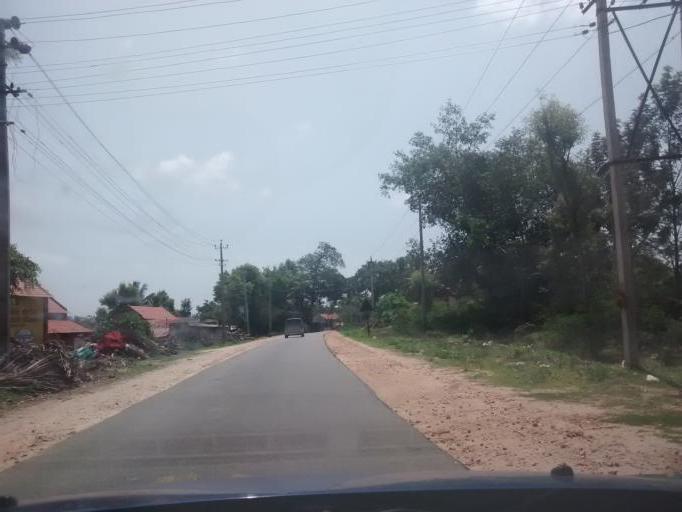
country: IN
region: Karnataka
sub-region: Mandya
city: Krishnarajpet
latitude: 12.5753
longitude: 76.3137
